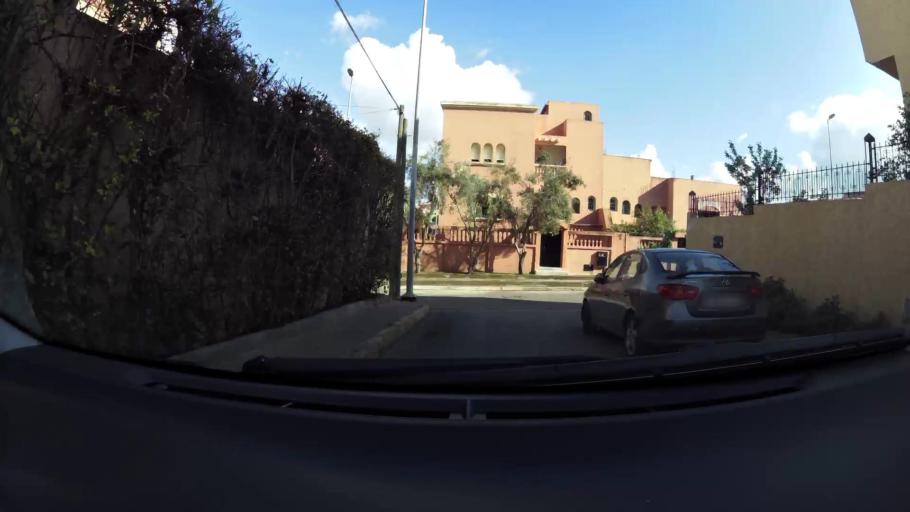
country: MA
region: Chaouia-Ouardigha
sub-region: Settat Province
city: Settat
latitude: 33.0117
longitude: -7.6320
